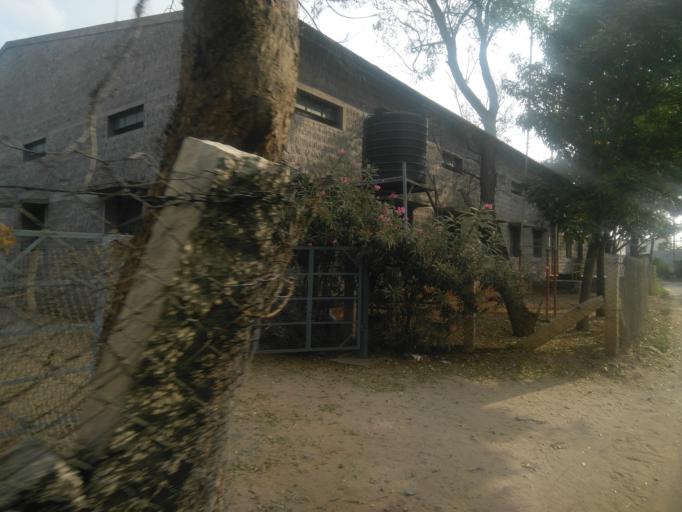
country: IN
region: Tamil Nadu
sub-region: Coimbatore
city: Periyanayakkanpalaiyam
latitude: 11.0771
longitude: 76.9234
